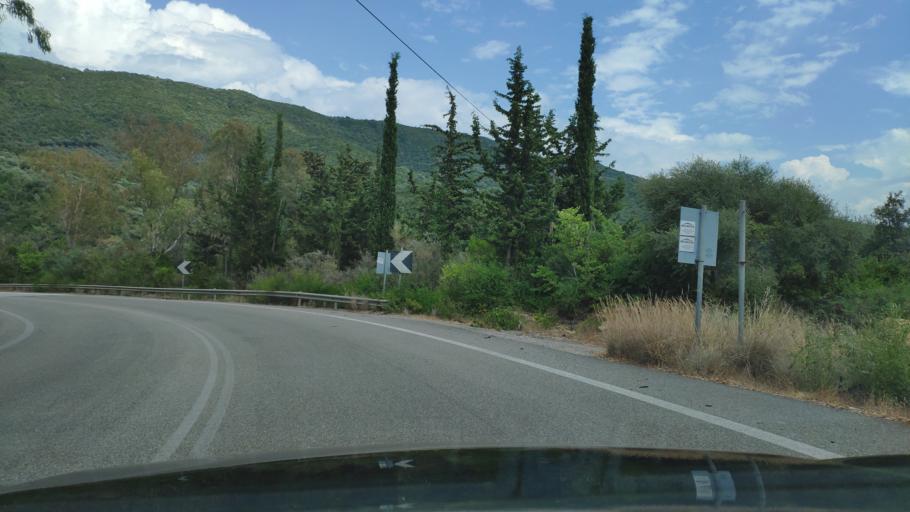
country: GR
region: West Greece
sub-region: Nomos Aitolias kai Akarnanias
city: Menidi
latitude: 39.0245
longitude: 21.1281
